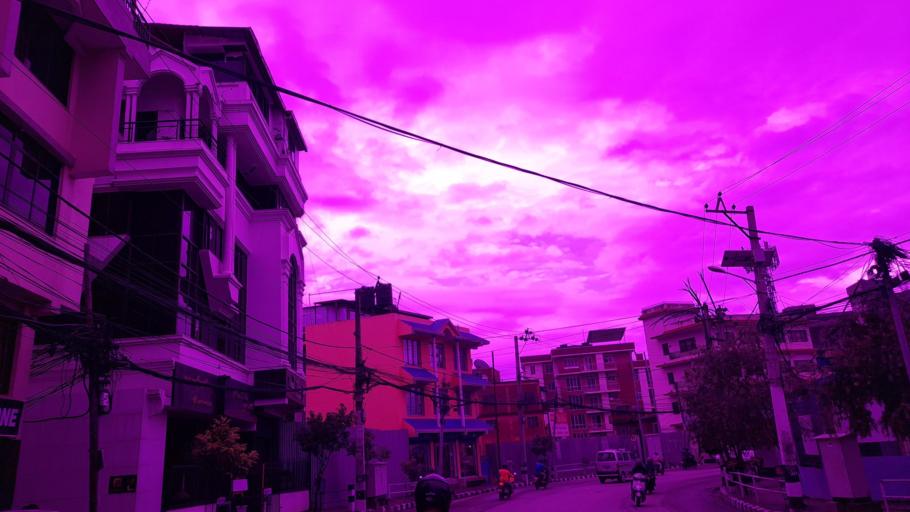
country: NP
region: Central Region
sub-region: Bagmati Zone
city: Kathmandu
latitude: 27.7288
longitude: 85.3250
